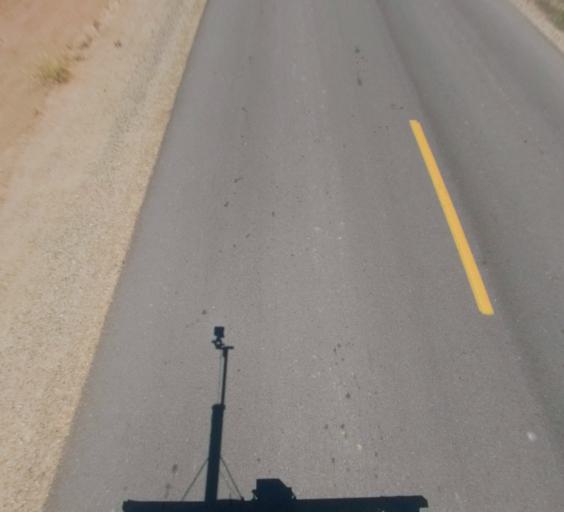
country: US
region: California
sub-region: Madera County
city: Madera Acres
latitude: 37.0482
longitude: -120.0019
